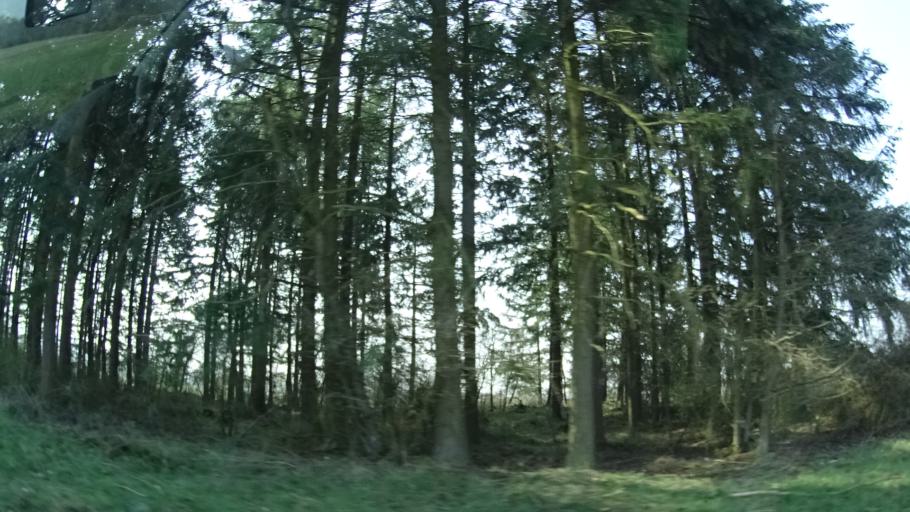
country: DE
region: Rheinland-Pfalz
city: Baumholder
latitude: 49.5981
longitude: 7.3498
